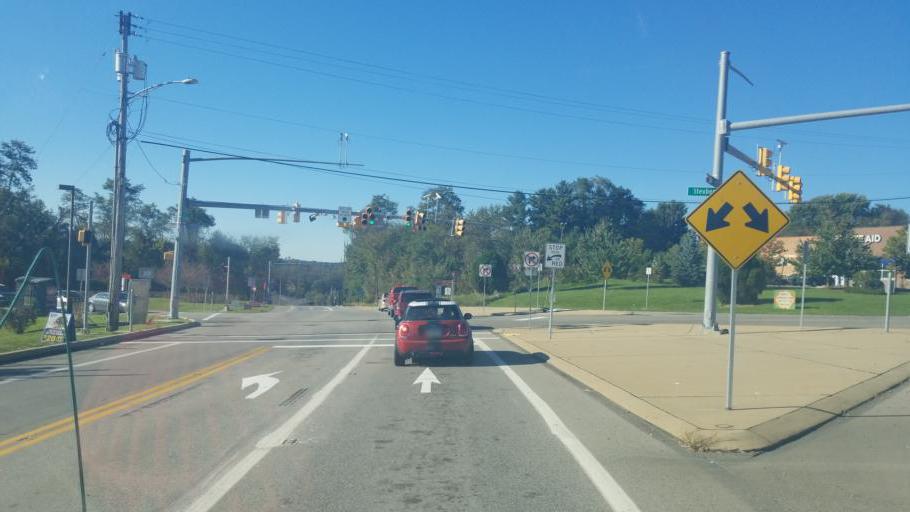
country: US
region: Pennsylvania
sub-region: Allegheny County
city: Imperial
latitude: 40.4415
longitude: -80.2392
